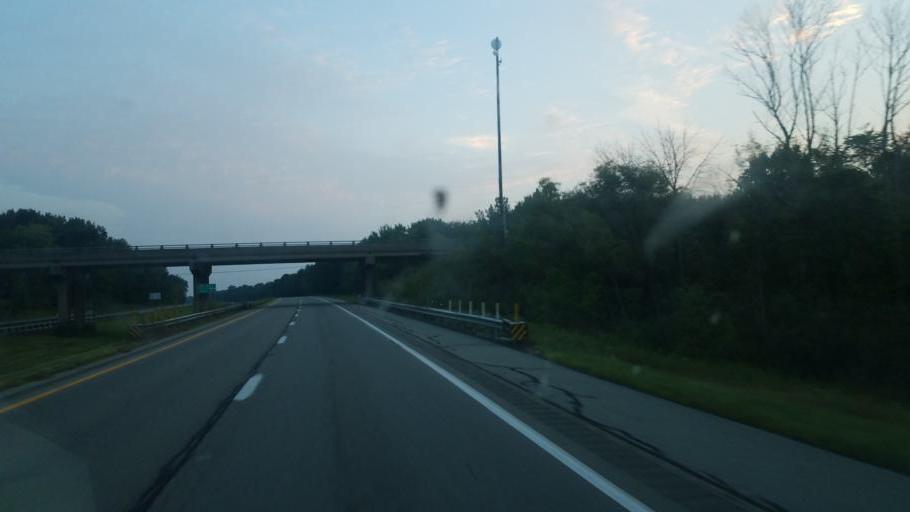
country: US
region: Pennsylvania
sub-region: Crawford County
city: Cochranton
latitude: 41.4906
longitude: -80.1663
